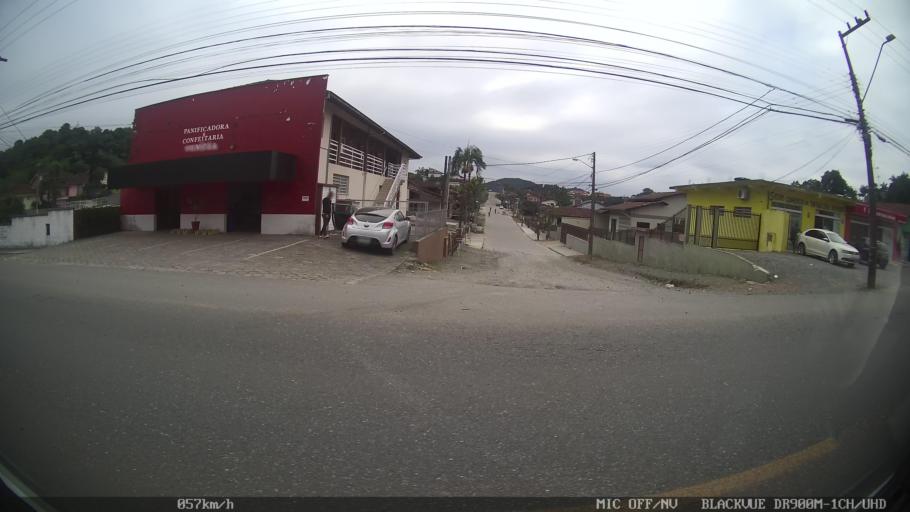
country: BR
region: Santa Catarina
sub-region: Joinville
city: Joinville
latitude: -26.3312
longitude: -48.8722
